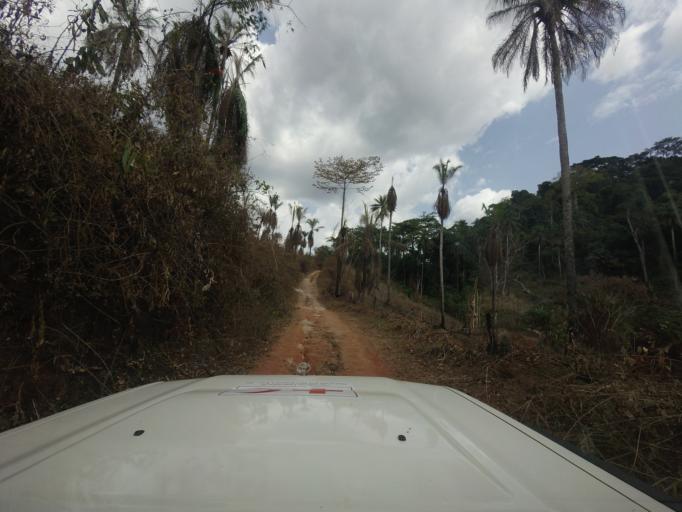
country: LR
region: Lofa
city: Voinjama
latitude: 8.3945
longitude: -9.6289
